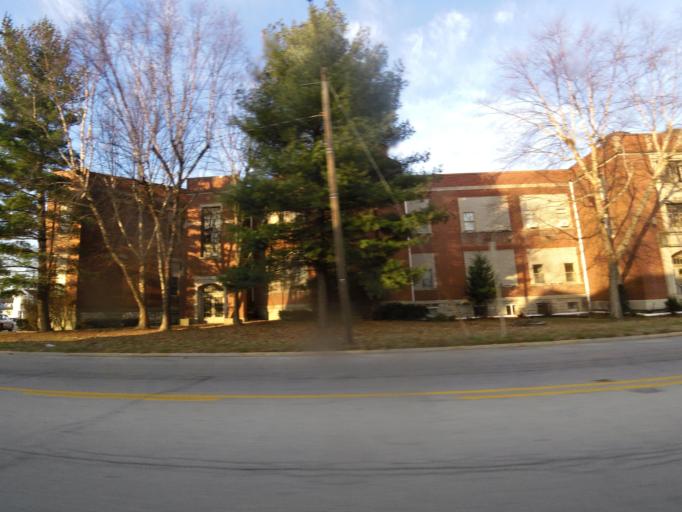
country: US
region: Illinois
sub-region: Fayette County
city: Vandalia
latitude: 38.9633
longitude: -89.0933
